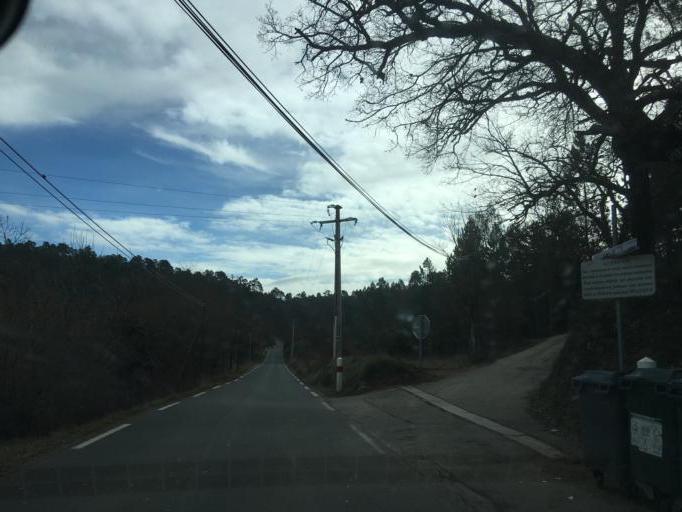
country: FR
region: Provence-Alpes-Cote d'Azur
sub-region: Departement du Var
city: Bras
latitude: 43.4596
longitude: 5.9655
